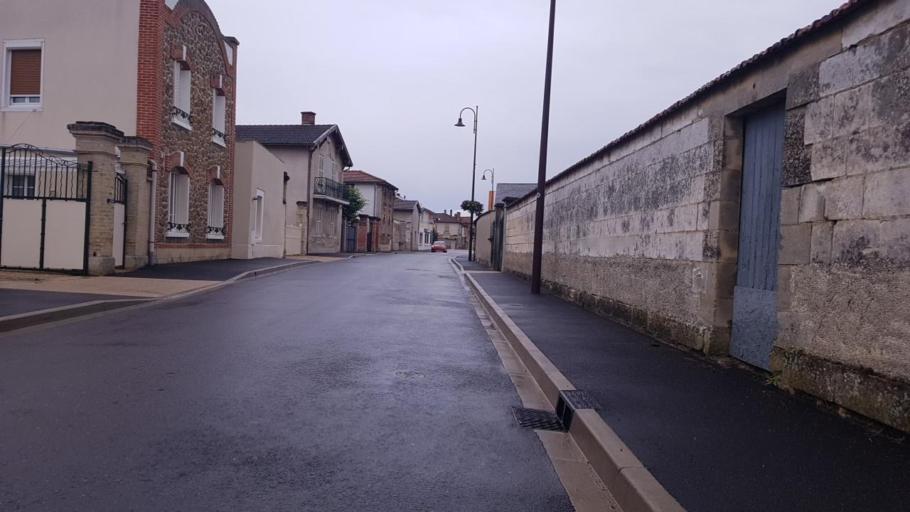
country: FR
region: Champagne-Ardenne
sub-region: Departement de la Marne
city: Sarry
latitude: 48.9177
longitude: 4.4079
